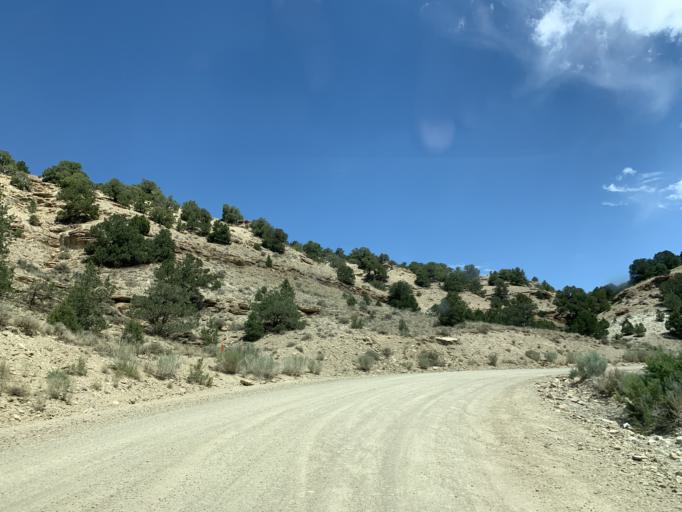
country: US
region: Utah
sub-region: Duchesne County
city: Duchesne
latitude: 39.8739
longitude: -110.2413
